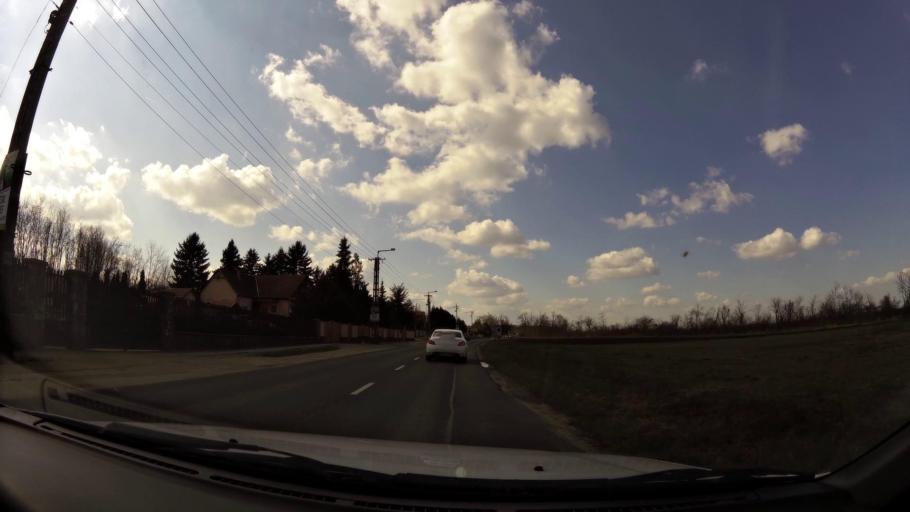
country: HU
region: Pest
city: Szentmartonkata
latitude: 47.4489
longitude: 19.6840
